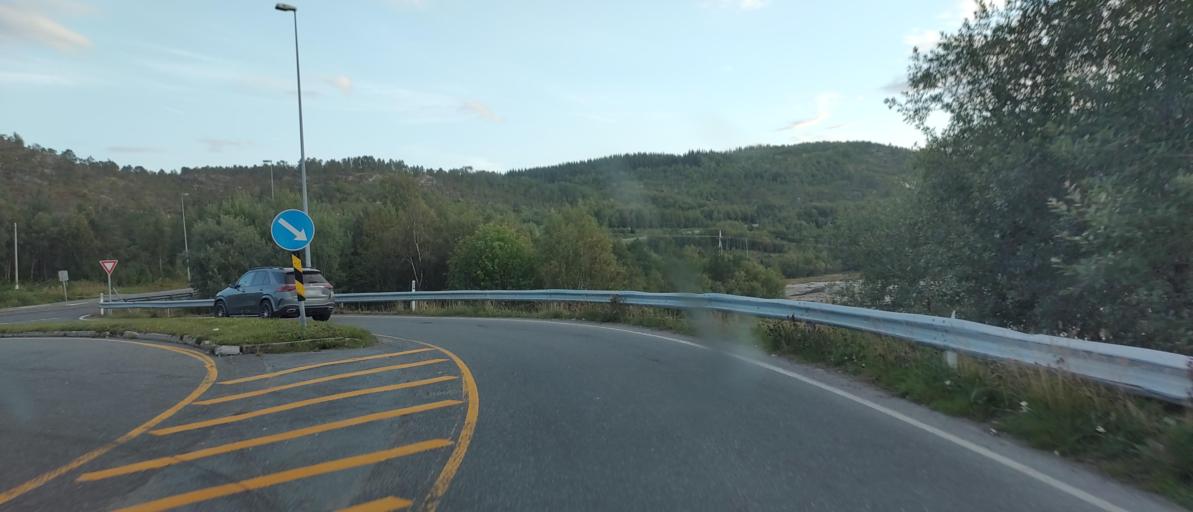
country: NO
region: Nordland
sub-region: Lodingen
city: Lodingen
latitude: 68.2220
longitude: 16.0710
